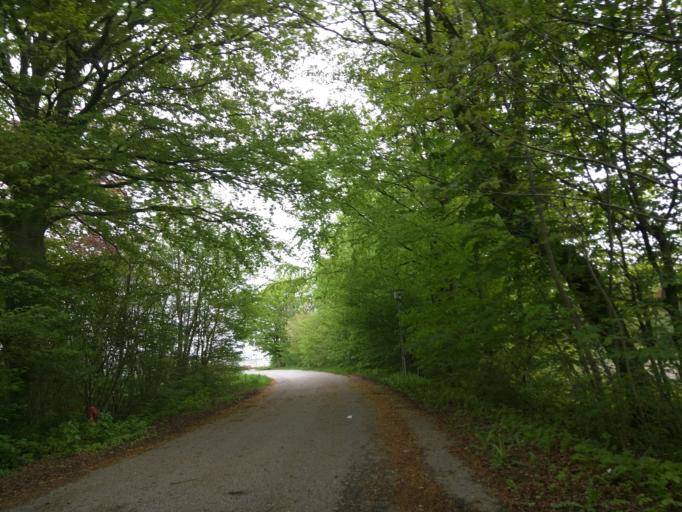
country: DK
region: Central Jutland
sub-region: Viborg Kommune
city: Viborg
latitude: 56.4435
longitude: 9.3685
